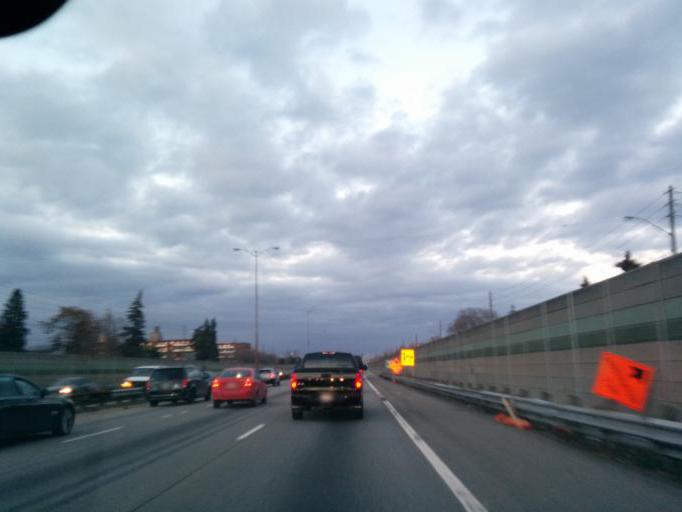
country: CA
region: Ontario
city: Mississauga
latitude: 43.5772
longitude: -79.5899
